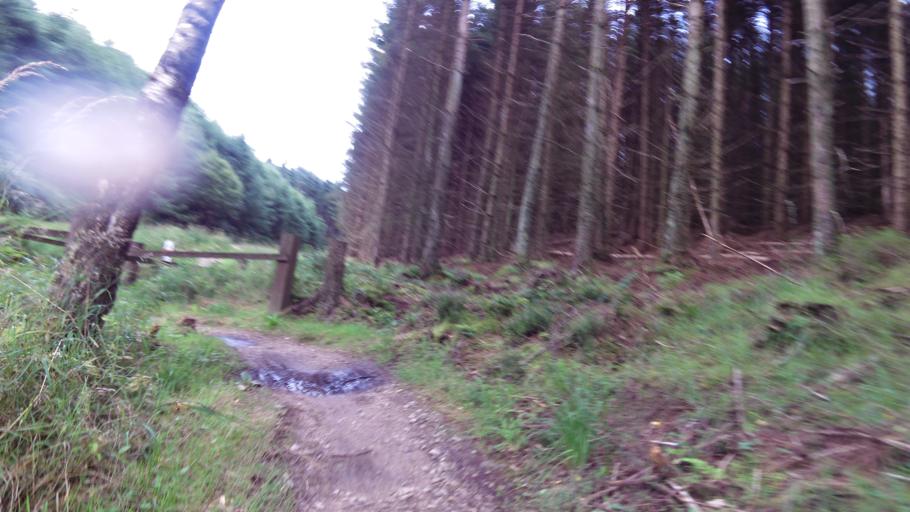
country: GB
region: England
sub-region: North Yorkshire
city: Thornton Dale
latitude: 54.2831
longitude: -0.6792
